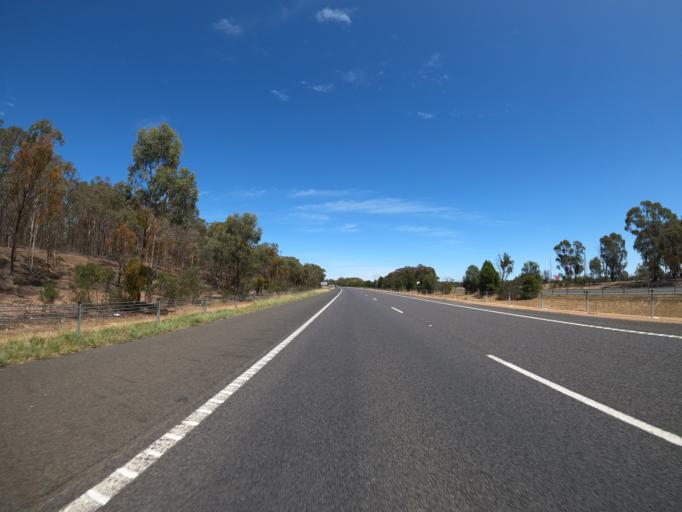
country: AU
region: Victoria
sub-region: Benalla
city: Benalla
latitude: -36.5763
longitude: 145.9295
